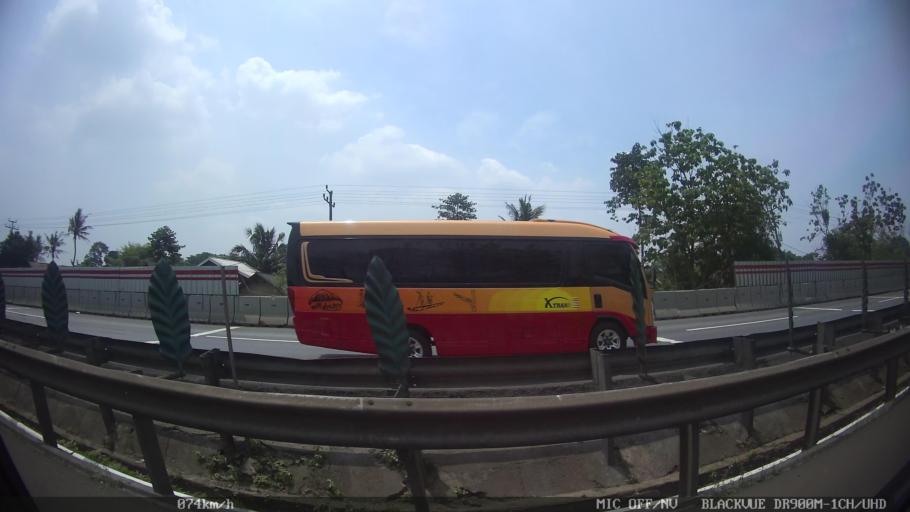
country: ID
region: West Java
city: Kresek
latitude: -6.1497
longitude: 106.3044
